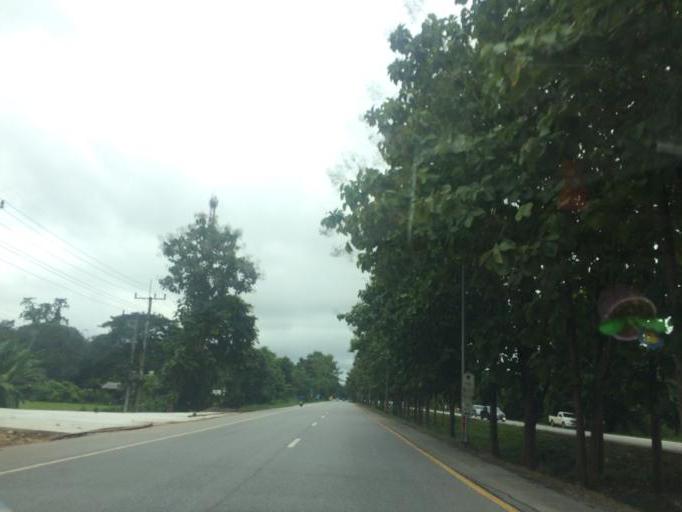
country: TH
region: Chiang Rai
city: Mae Lao
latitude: 19.8020
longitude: 99.7538
